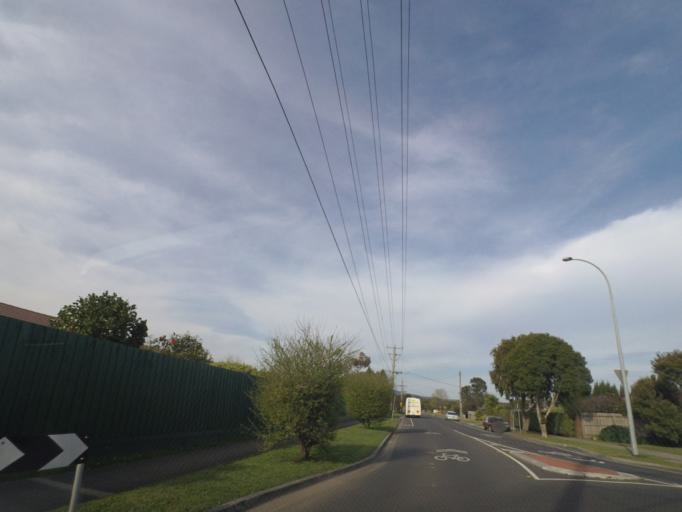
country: AU
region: Victoria
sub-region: Knox
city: Scoresby
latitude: -37.8890
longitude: 145.2287
